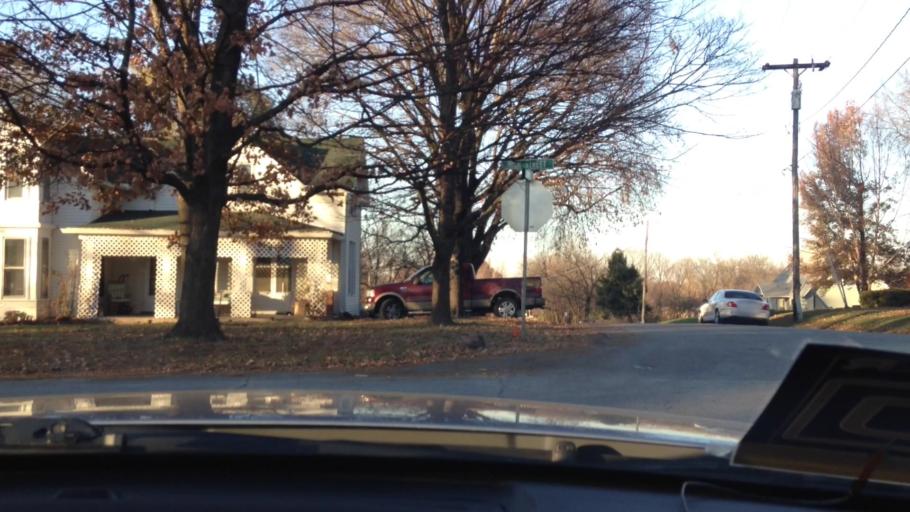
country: US
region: Kansas
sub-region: Leavenworth County
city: Leavenworth
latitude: 39.3121
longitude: -94.9347
